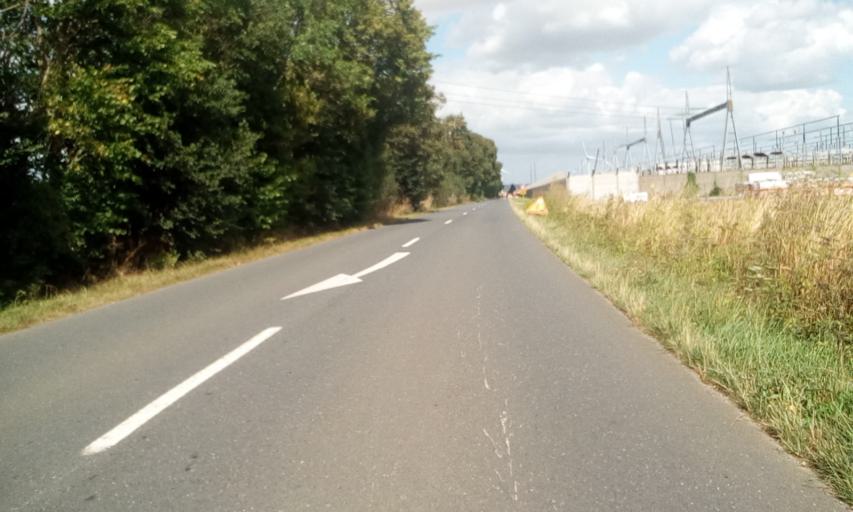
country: FR
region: Lower Normandy
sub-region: Departement du Calvados
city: Bourguebus
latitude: 49.1062
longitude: -0.2674
